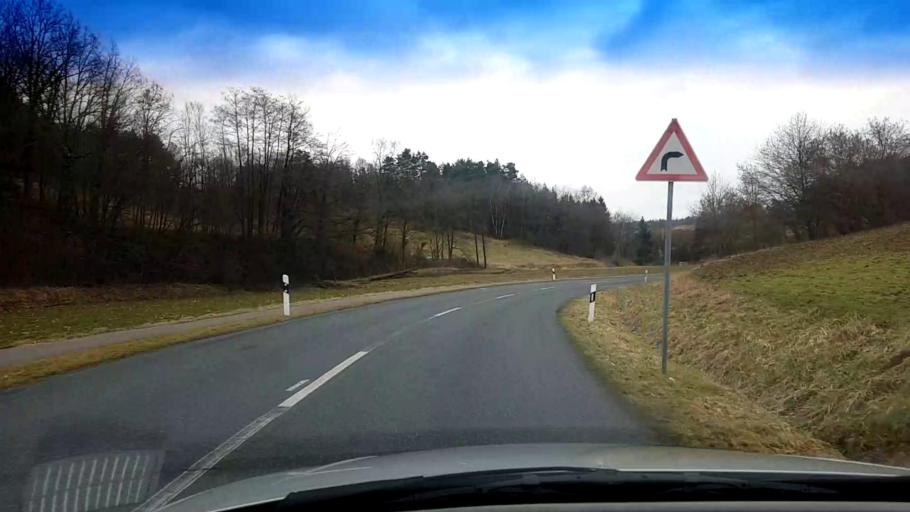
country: DE
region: Bavaria
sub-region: Upper Franconia
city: Bischberg
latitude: 49.9031
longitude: 10.8172
